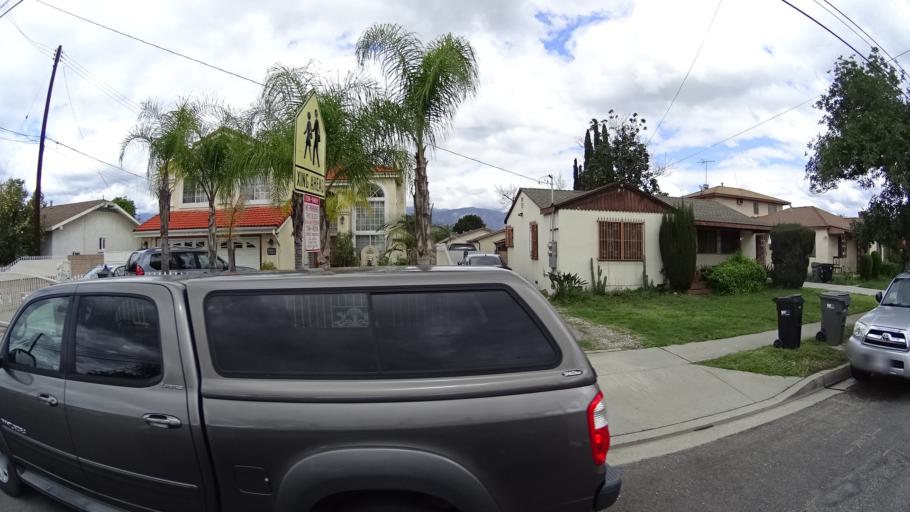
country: US
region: California
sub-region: Los Angeles County
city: Baldwin Park
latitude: 34.0923
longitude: -117.9660
